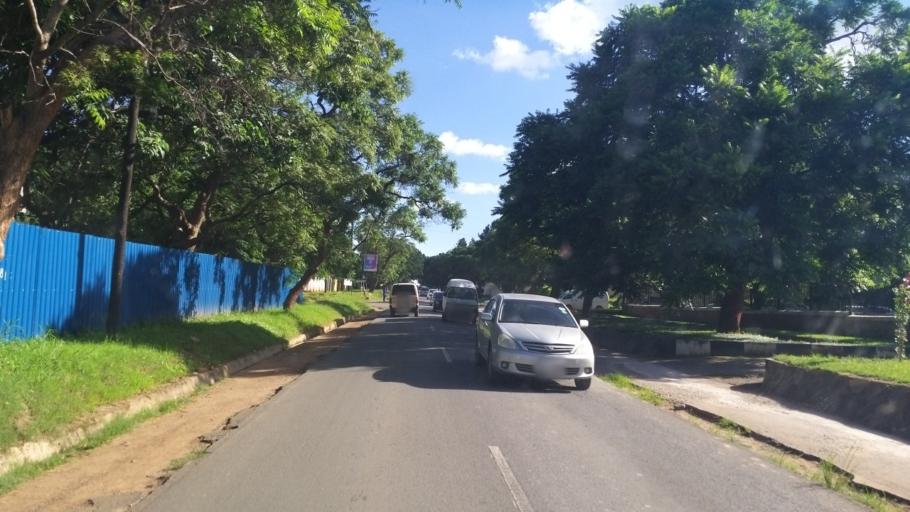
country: ZM
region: Lusaka
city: Lusaka
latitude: -15.4201
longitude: 28.3125
